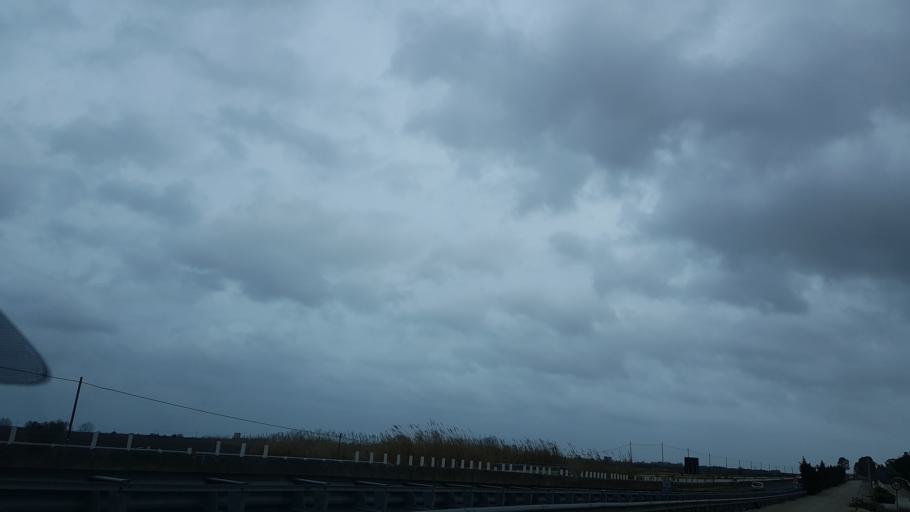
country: IT
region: Apulia
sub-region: Provincia di Brindisi
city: Brindisi
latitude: 40.6683
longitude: 17.8655
